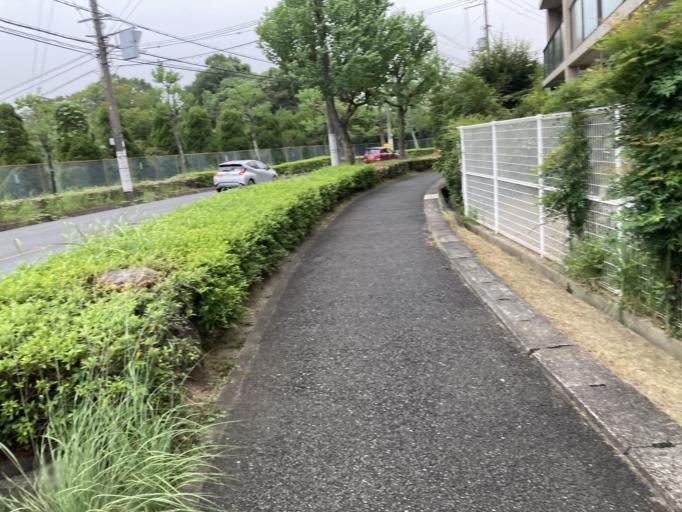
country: JP
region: Nara
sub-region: Ikoma-shi
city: Ikoma
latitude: 34.6538
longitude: 135.7096
